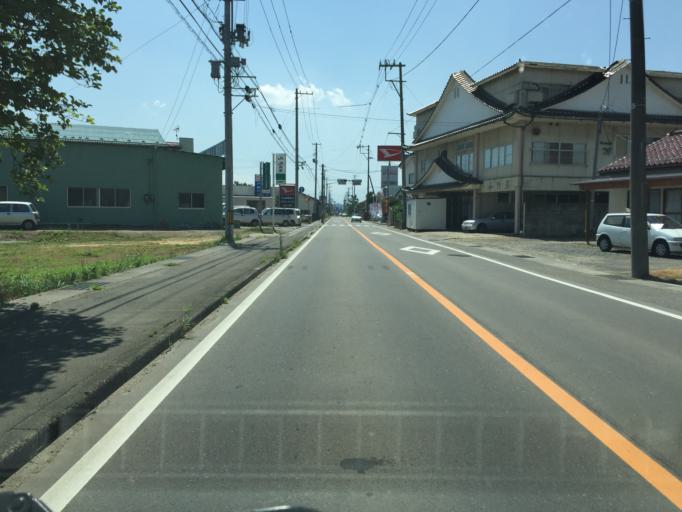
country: JP
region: Fukushima
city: Hobaramachi
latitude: 37.8307
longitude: 140.5640
